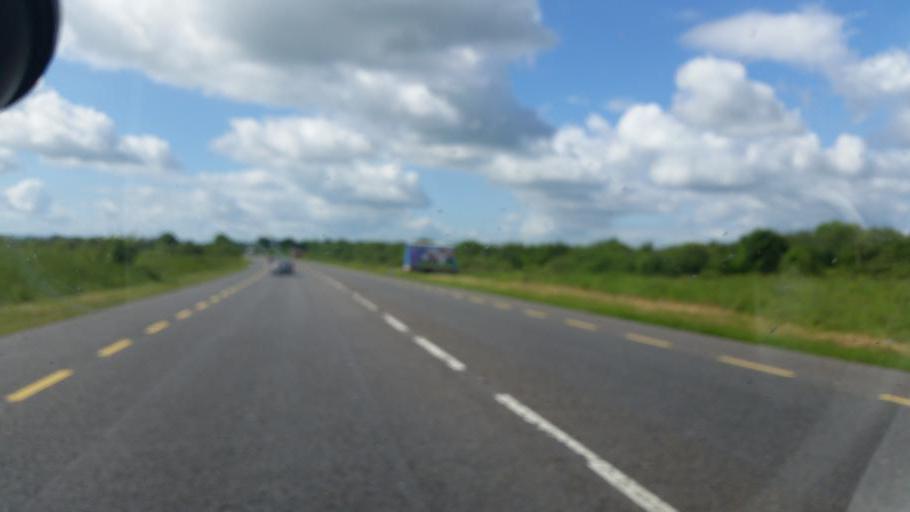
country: IE
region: Leinster
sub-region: An Iarmhi
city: Kilbeggan
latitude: 53.3523
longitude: -7.4971
